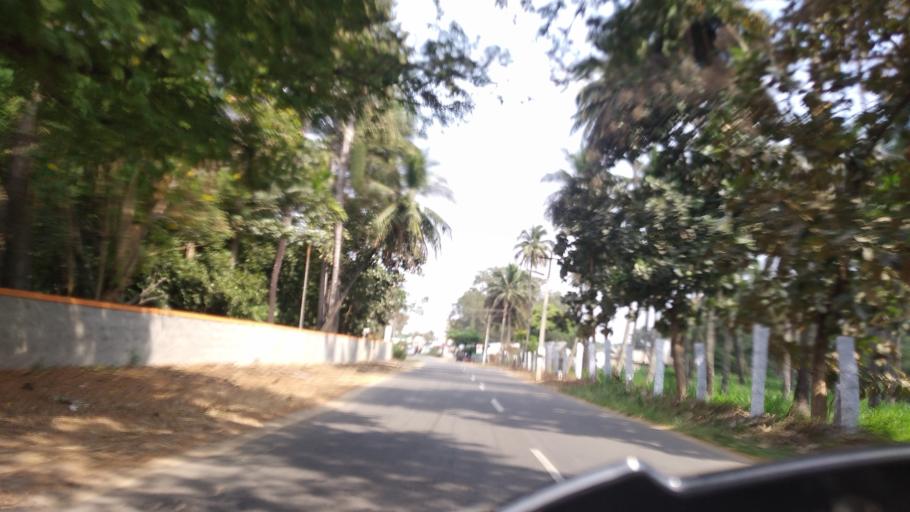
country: IN
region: Tamil Nadu
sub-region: Coimbatore
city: Perur
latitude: 10.9579
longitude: 76.7559
